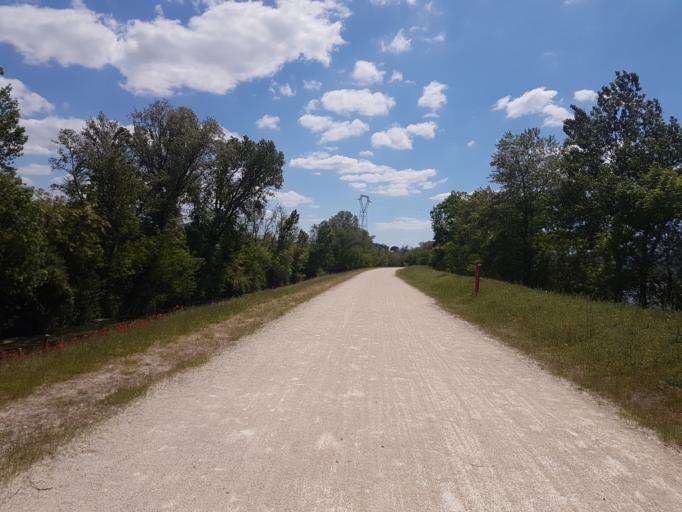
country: FR
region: Rhone-Alpes
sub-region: Departement de l'Ardeche
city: Tournon-sur-Rhone
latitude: 45.0556
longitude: 4.8623
